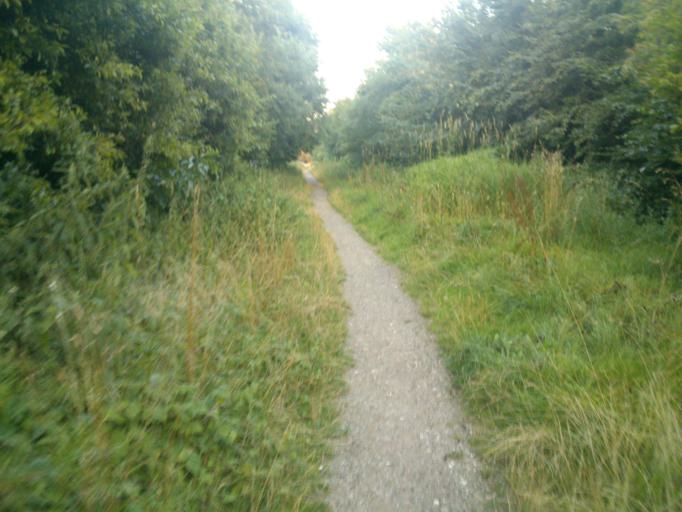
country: DK
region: South Denmark
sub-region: Fredericia Kommune
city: Fredericia
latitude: 55.5754
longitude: 9.7106
